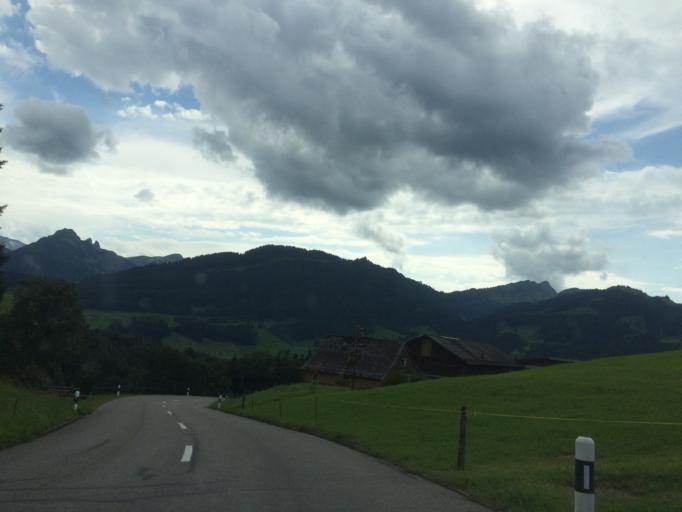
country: CH
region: Saint Gallen
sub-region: Wahlkreis Toggenburg
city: Krummenau
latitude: 47.2373
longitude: 9.2034
